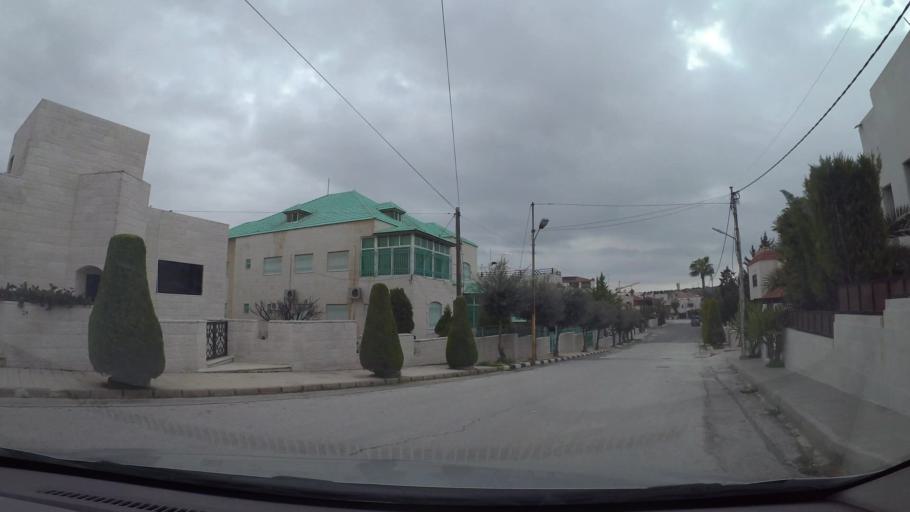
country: JO
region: Amman
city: Wadi as Sir
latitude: 31.9877
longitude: 35.8341
